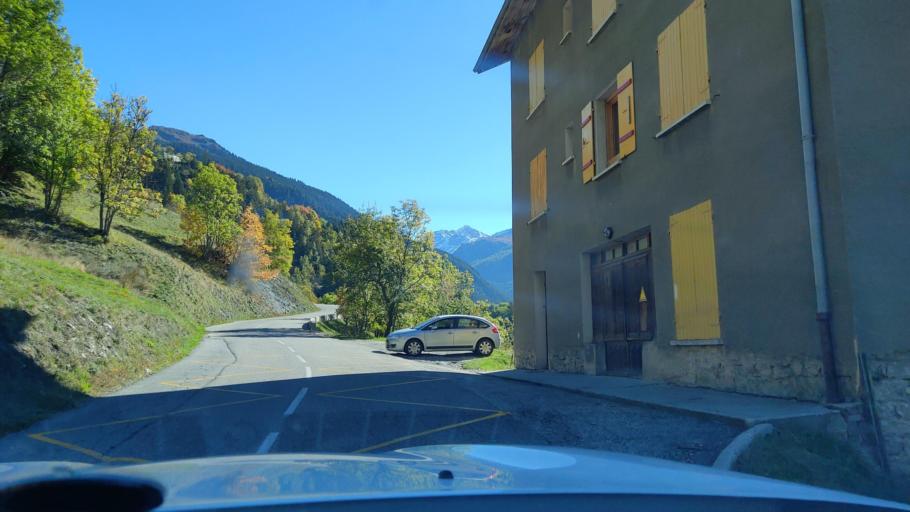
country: FR
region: Rhone-Alpes
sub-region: Departement de la Savoie
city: Seez
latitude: 45.6139
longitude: 6.8483
